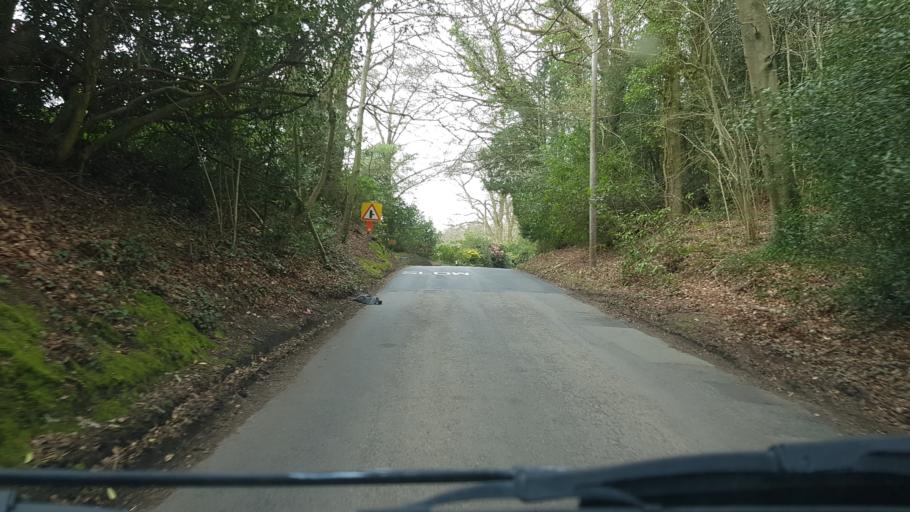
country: GB
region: England
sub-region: Surrey
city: Cranleigh
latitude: 51.1675
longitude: -0.4525
